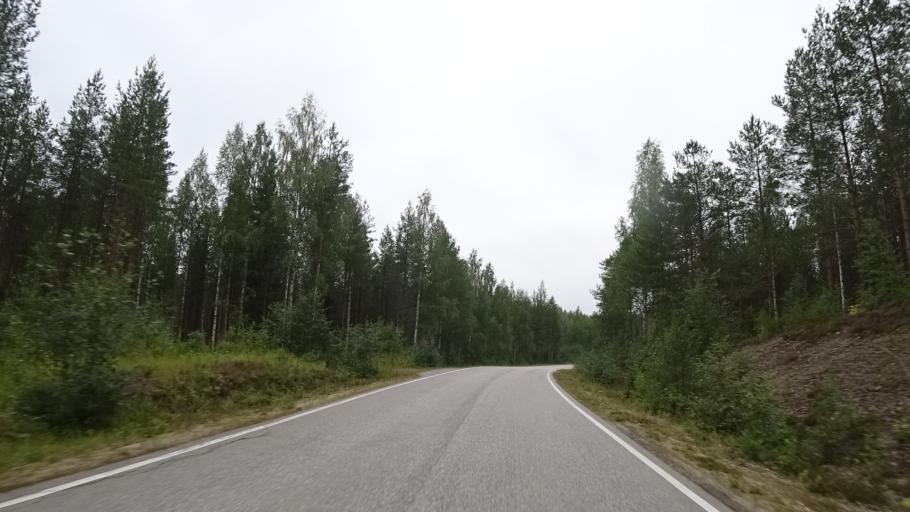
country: FI
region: North Karelia
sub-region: Pielisen Karjala
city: Lieksa
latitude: 63.3246
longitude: 30.2356
